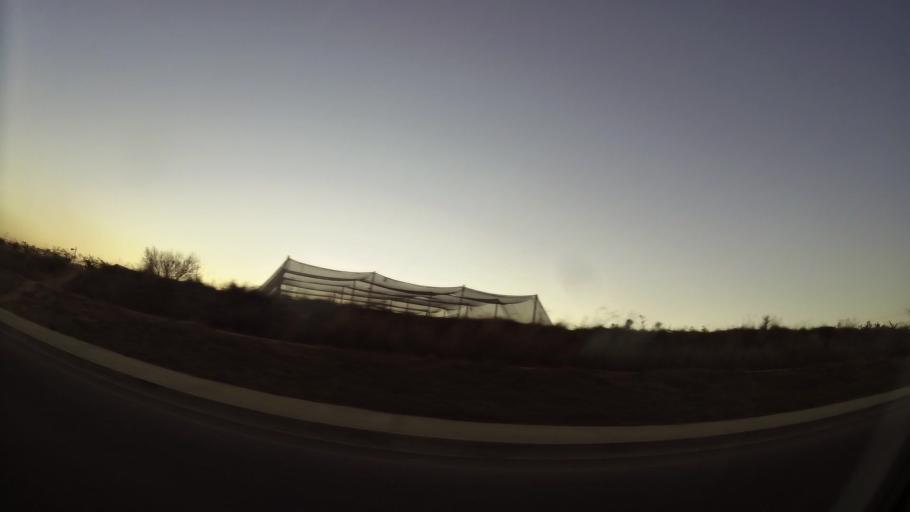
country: ZA
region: Gauteng
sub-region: City of Johannesburg Metropolitan Municipality
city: Diepsloot
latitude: -25.9733
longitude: 28.0209
